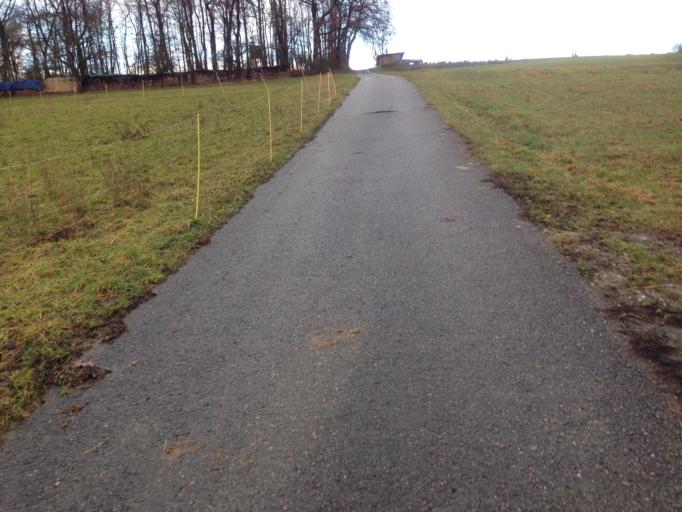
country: DE
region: Baden-Wuerttemberg
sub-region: Karlsruhe Region
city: Billigheim
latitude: 49.4028
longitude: 9.2292
